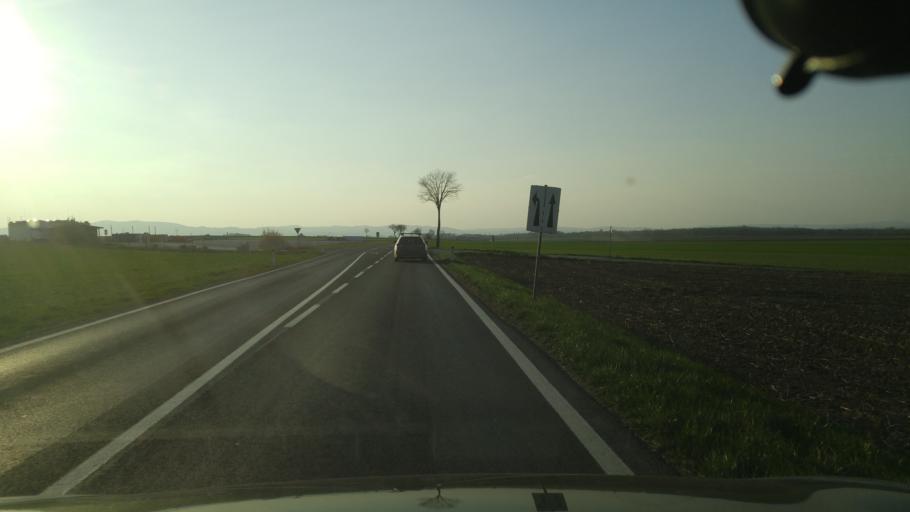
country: AT
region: Lower Austria
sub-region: Politischer Bezirk Wien-Umgebung
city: Gramatneusiedl
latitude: 48.0396
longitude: 16.4725
